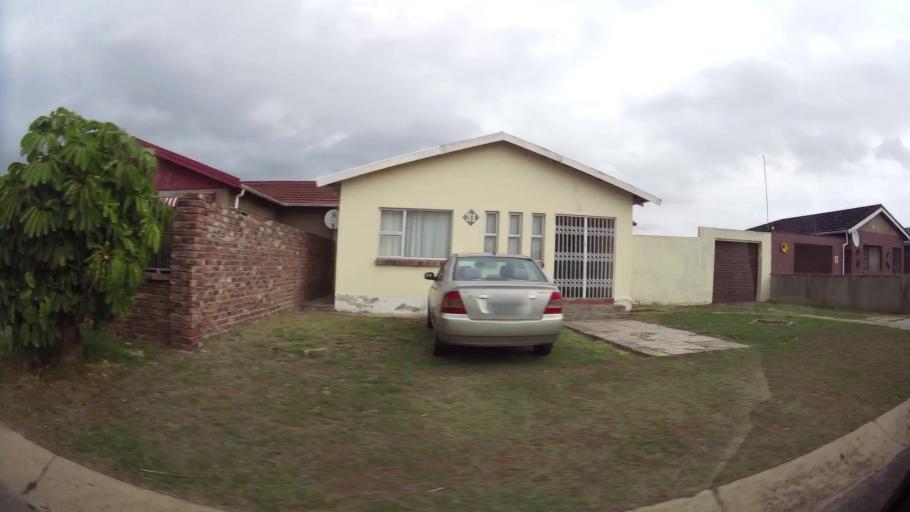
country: ZA
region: Eastern Cape
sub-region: Nelson Mandela Bay Metropolitan Municipality
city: Port Elizabeth
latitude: -33.8978
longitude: 25.5636
